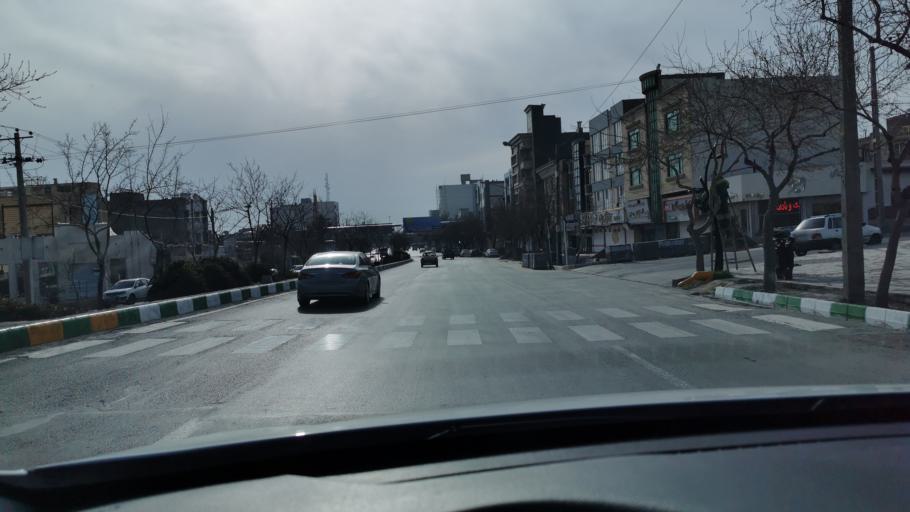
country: IR
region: Razavi Khorasan
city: Mashhad
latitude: 36.2937
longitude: 59.5328
